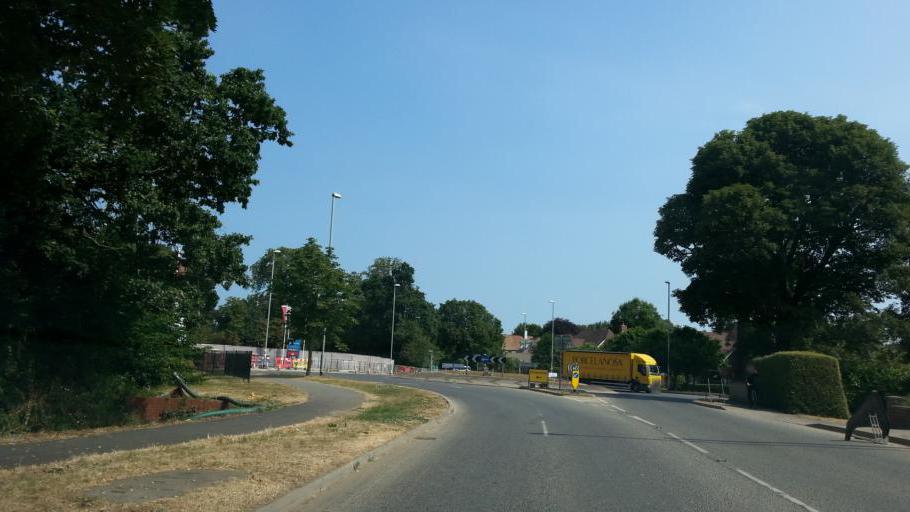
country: GB
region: England
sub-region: Cambridgeshire
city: Brampton
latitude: 52.3166
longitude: -0.2212
